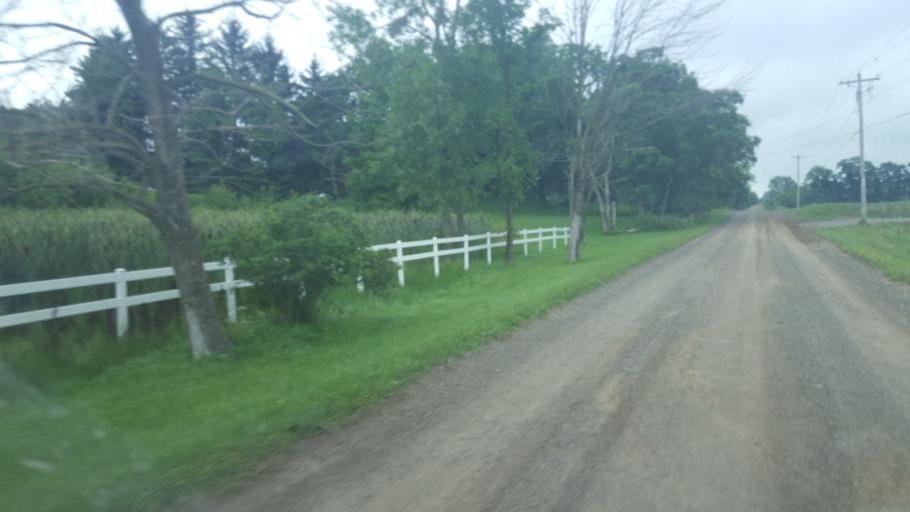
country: US
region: Ohio
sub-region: Morrow County
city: Mount Gilead
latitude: 40.4232
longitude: -82.7730
